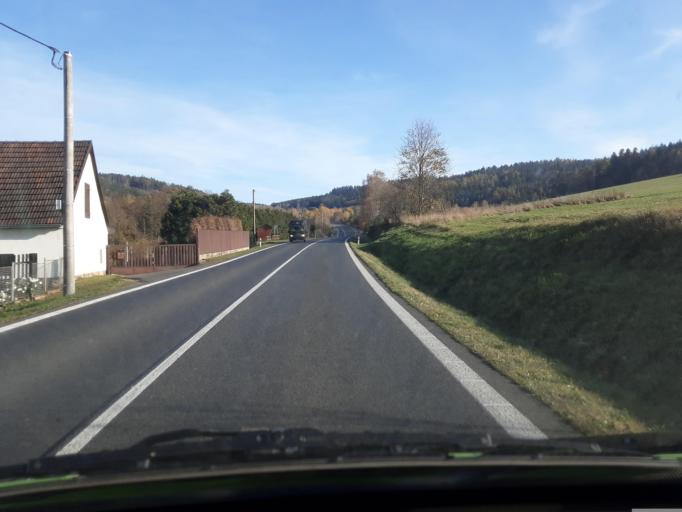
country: CZ
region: Plzensky
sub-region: Okres Klatovy
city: Kolinec
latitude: 49.3567
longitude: 13.3979
